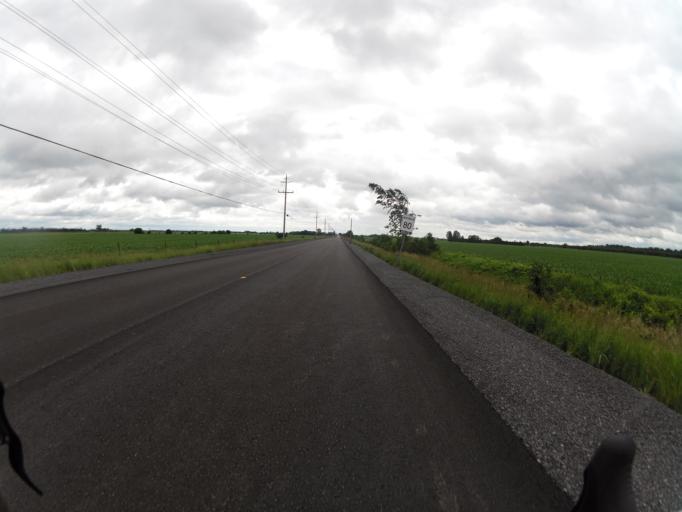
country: CA
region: Ontario
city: Bells Corners
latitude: 45.2472
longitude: -75.8847
